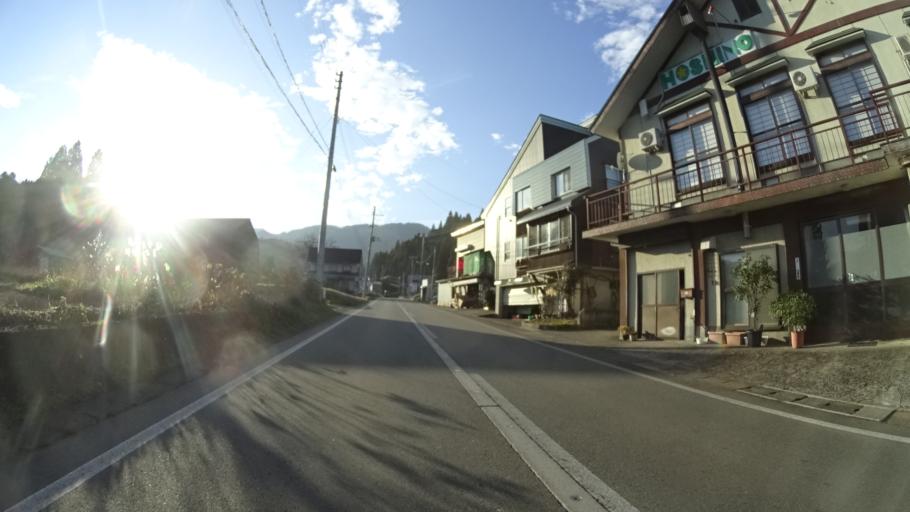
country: JP
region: Niigata
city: Shiozawa
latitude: 36.9877
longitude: 138.7994
